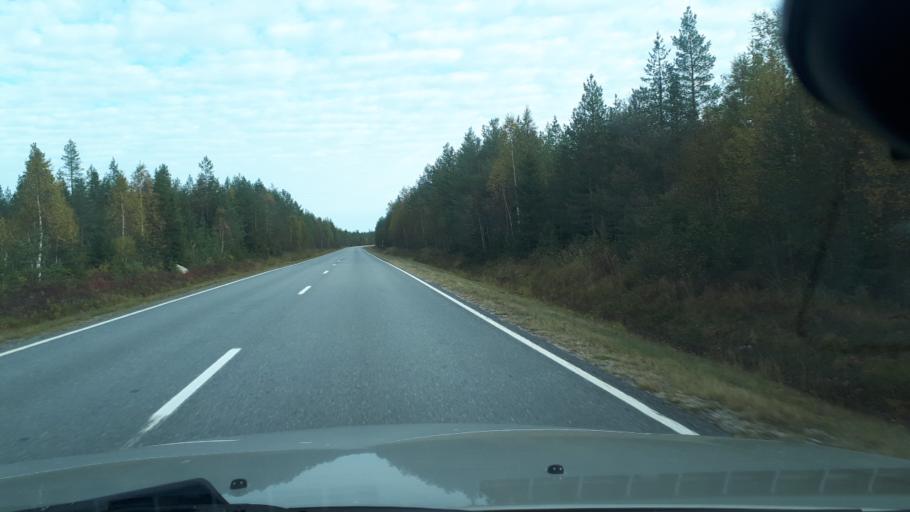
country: FI
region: Northern Ostrobothnia
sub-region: Oulu
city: Yli-Ii
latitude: 65.9063
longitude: 25.7387
